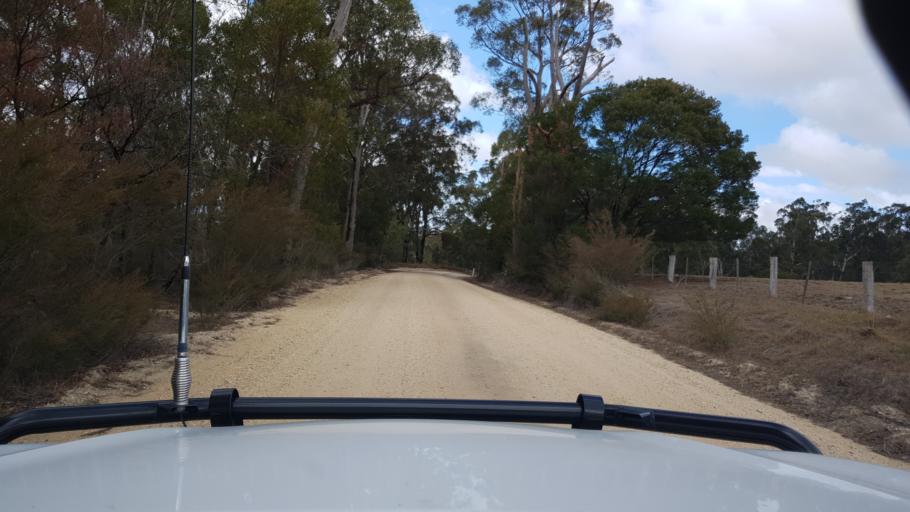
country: AU
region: Victoria
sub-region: East Gippsland
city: Bairnsdale
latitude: -37.7424
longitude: 147.6054
